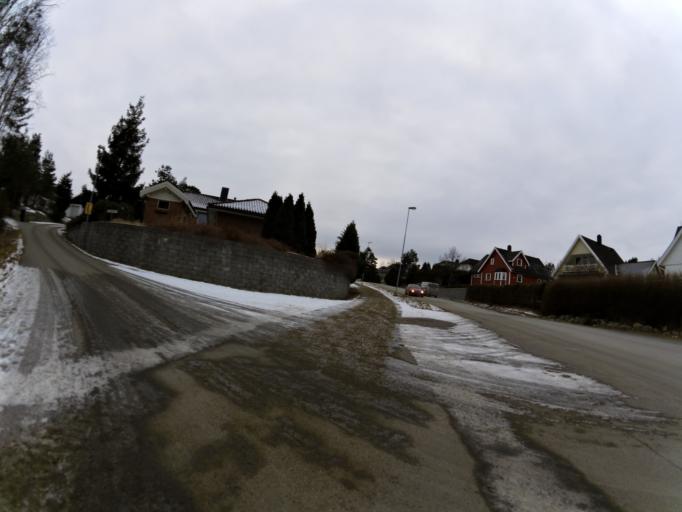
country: NO
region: Ostfold
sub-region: Fredrikstad
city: Fredrikstad
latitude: 59.1978
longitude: 10.8758
